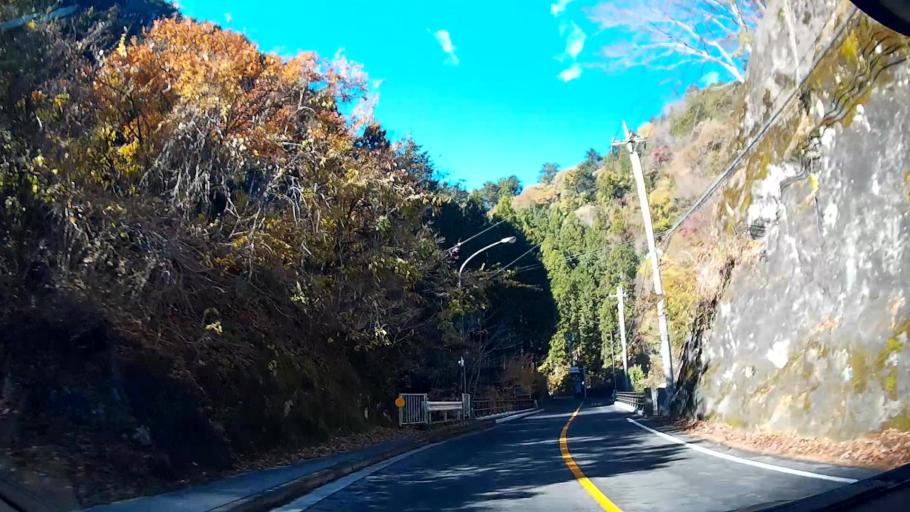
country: JP
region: Yamanashi
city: Uenohara
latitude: 35.7045
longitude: 139.1181
